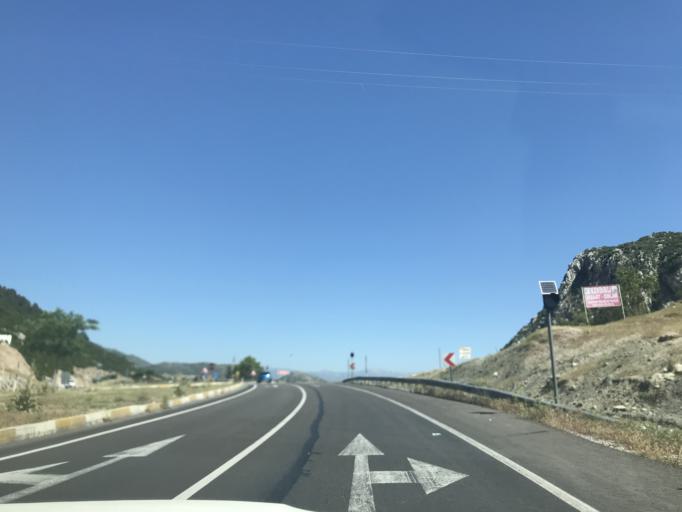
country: TR
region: Antalya
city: Dagbeli
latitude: 37.1694
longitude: 30.4980
